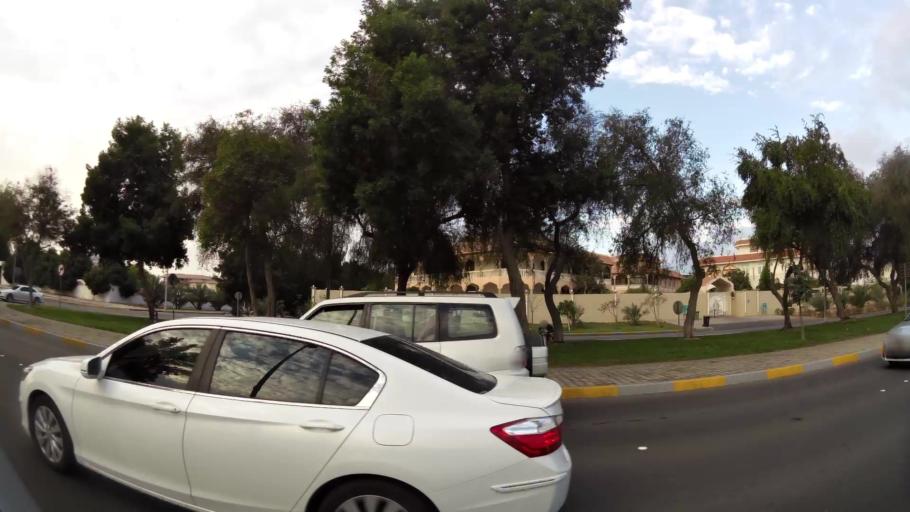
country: AE
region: Abu Dhabi
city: Abu Dhabi
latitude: 24.4464
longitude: 54.3651
